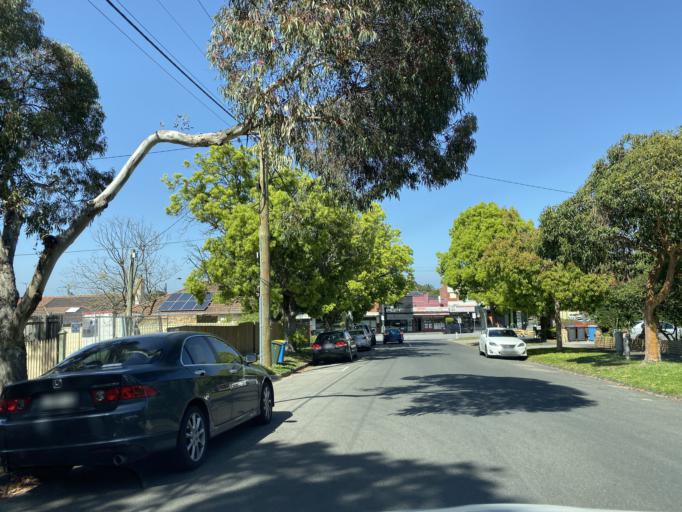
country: AU
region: Victoria
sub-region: Boroondara
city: Camberwell
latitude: -37.8460
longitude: 145.0634
